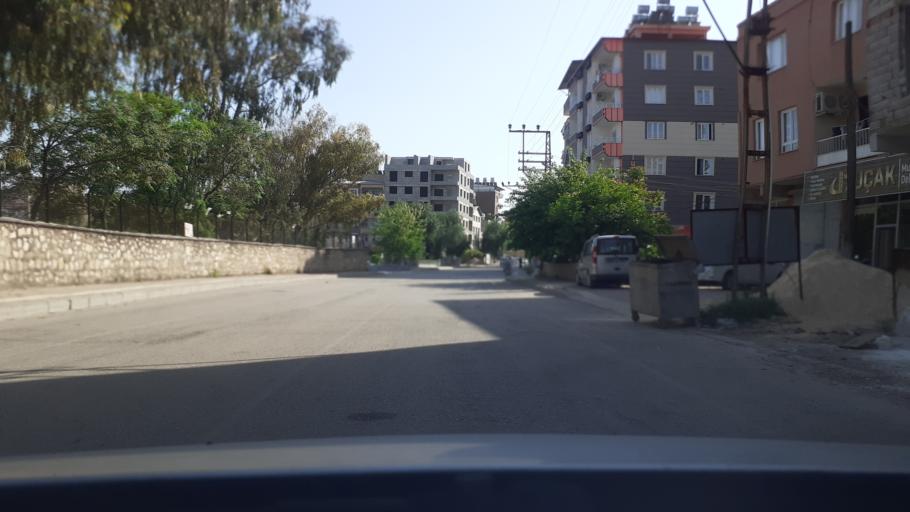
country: TR
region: Hatay
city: Kirikhan
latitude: 36.4933
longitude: 36.3671
